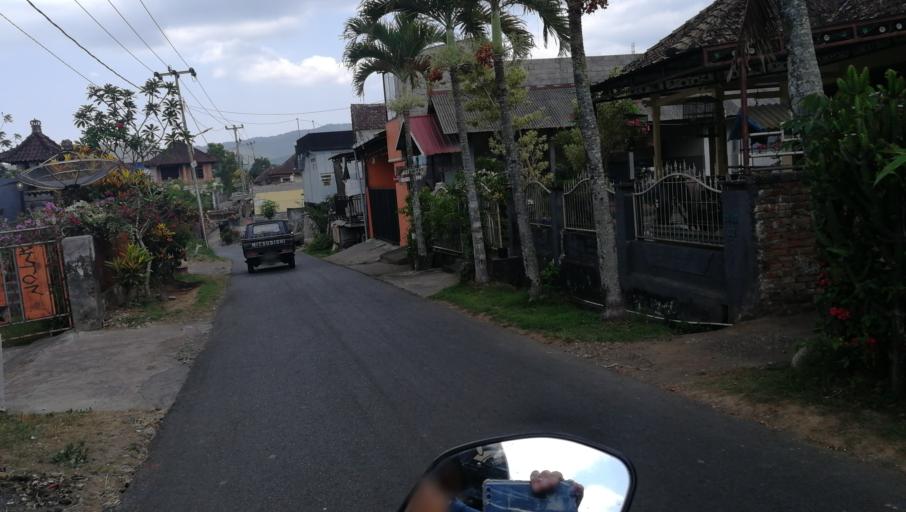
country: ID
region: Bali
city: Puspajati
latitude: -8.2769
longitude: 115.0260
